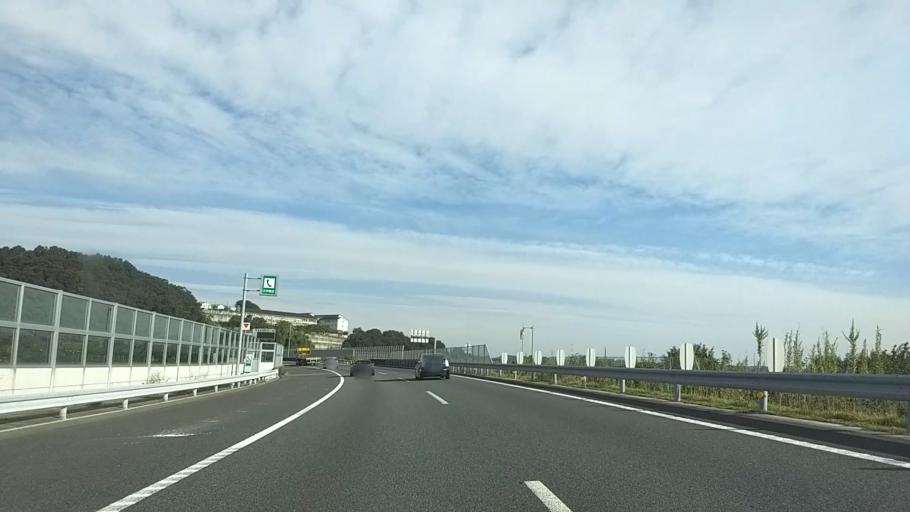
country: JP
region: Kanagawa
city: Zama
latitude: 35.5063
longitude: 139.3662
